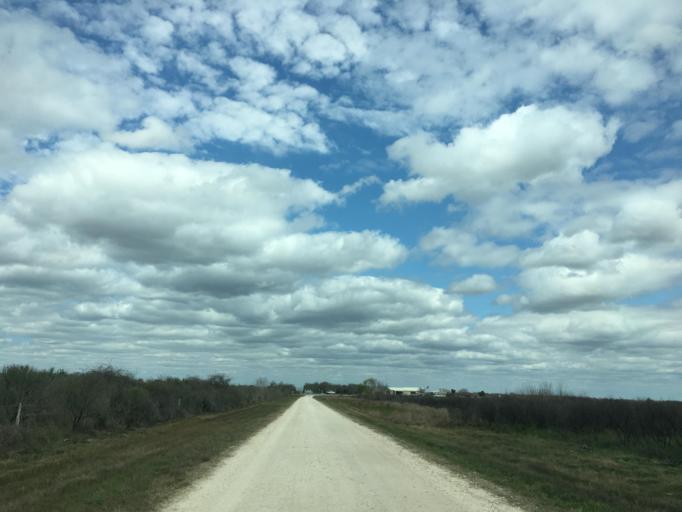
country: US
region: Texas
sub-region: Brazoria County
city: Oyster Creek
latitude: 29.0568
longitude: -95.2687
